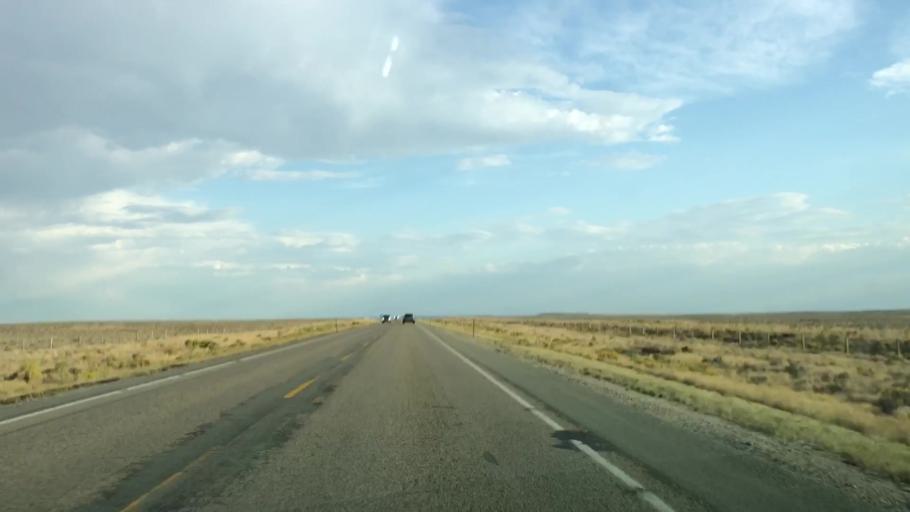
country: US
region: Wyoming
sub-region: Sublette County
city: Pinedale
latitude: 42.4107
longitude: -109.5524
